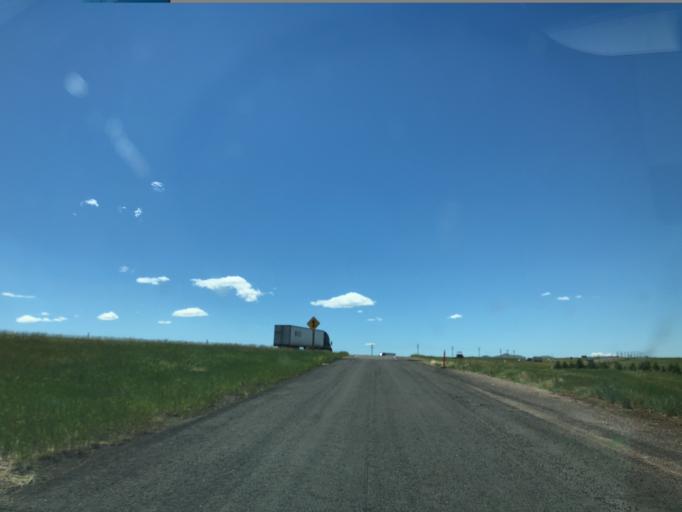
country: US
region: Wyoming
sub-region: Laramie County
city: Cheyenne
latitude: 41.1010
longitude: -105.0625
